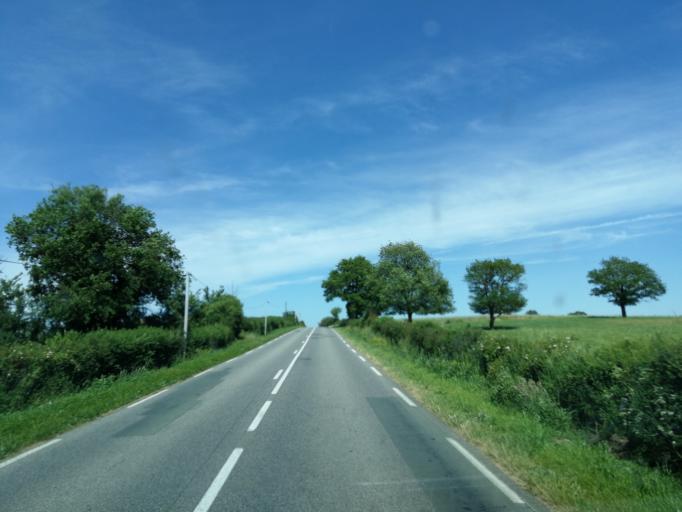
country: FR
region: Poitou-Charentes
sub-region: Departement des Deux-Sevres
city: Saint-Varent
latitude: 46.8846
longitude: -0.3162
